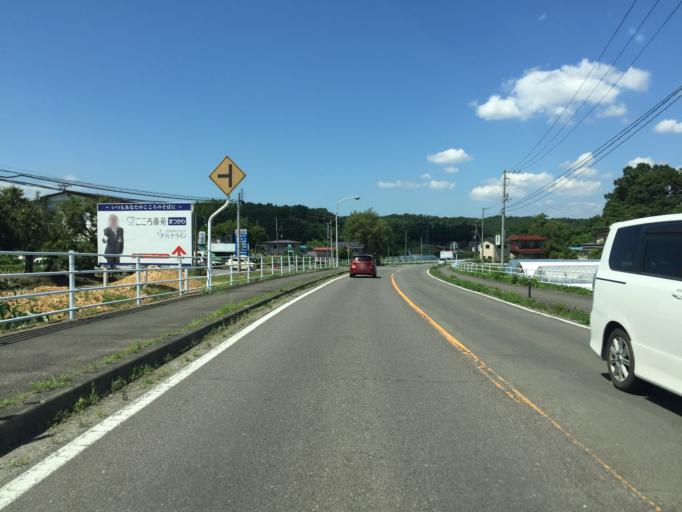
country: JP
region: Fukushima
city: Nihommatsu
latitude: 37.6251
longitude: 140.4608
